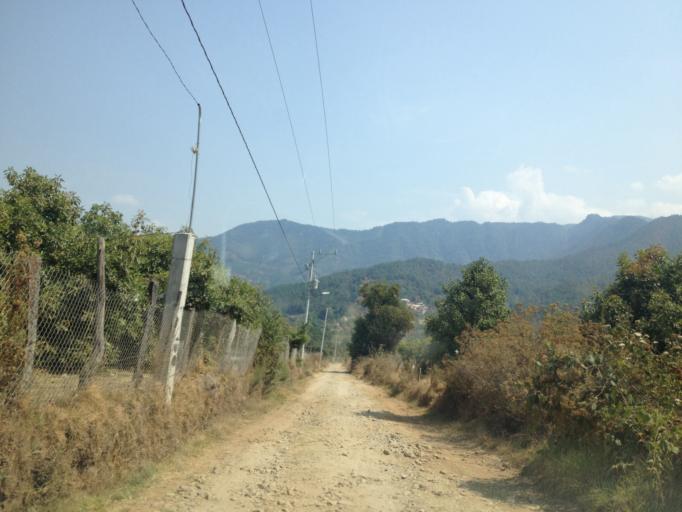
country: MX
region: Michoacan
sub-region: Zitacuaro
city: Macutzio
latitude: 19.4885
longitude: -100.3307
